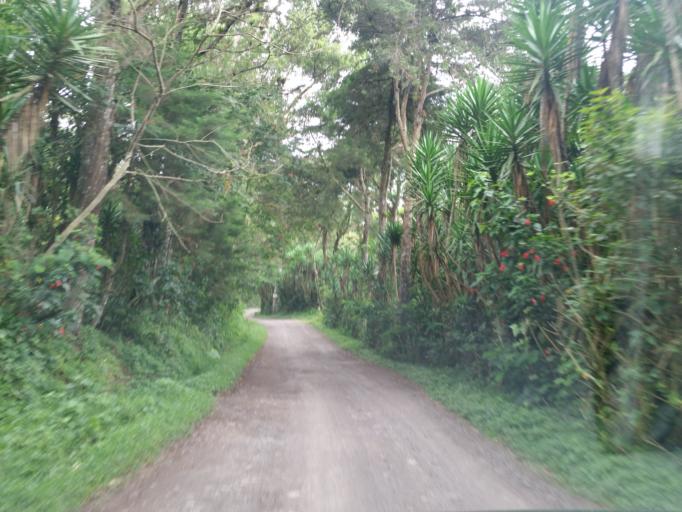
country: NI
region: Matagalpa
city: Matagalpa
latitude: 12.9973
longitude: -85.9189
